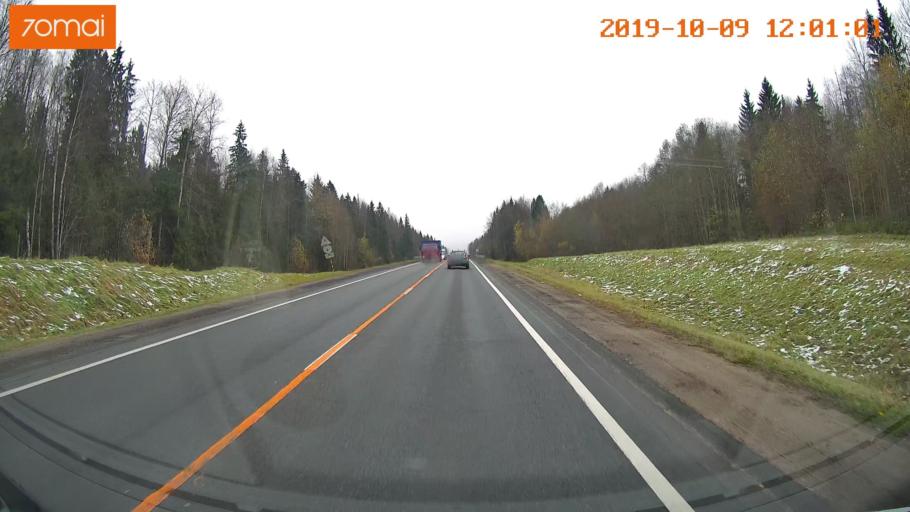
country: RU
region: Vologda
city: Gryazovets
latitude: 58.6927
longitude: 40.3015
